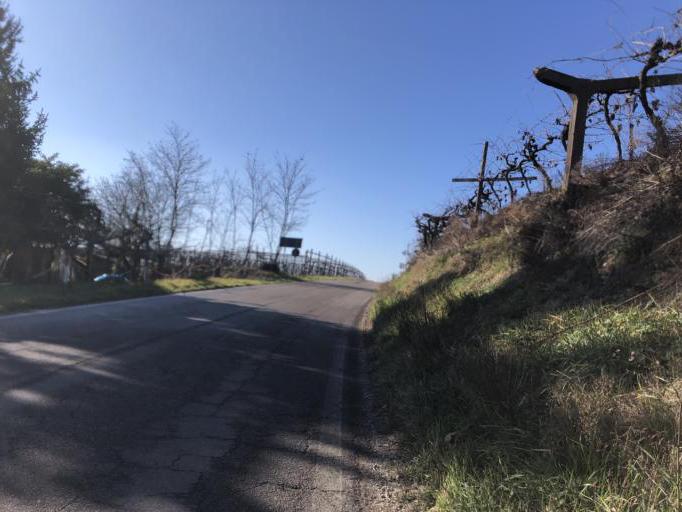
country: IT
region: Veneto
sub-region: Provincia di Verona
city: Sona
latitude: 45.4418
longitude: 10.8138
